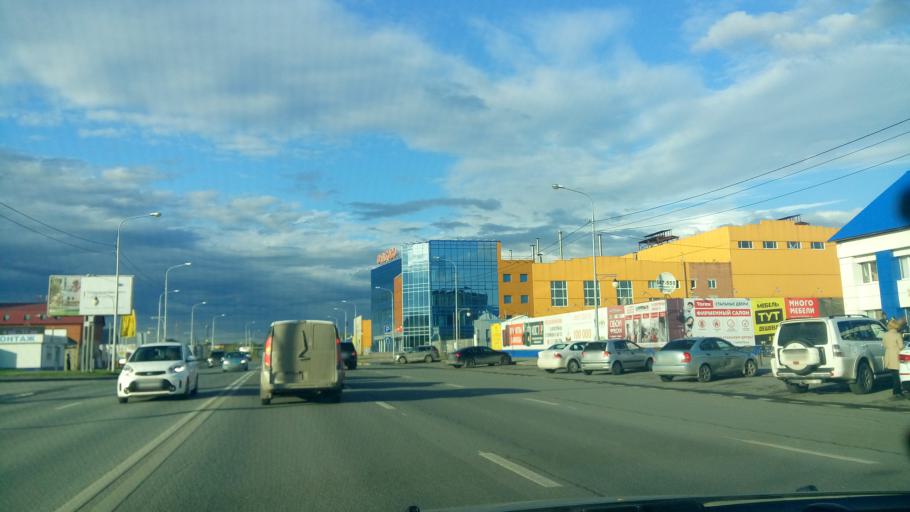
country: RU
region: Tjumen
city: Melioratorov
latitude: 57.1350
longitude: 65.6053
